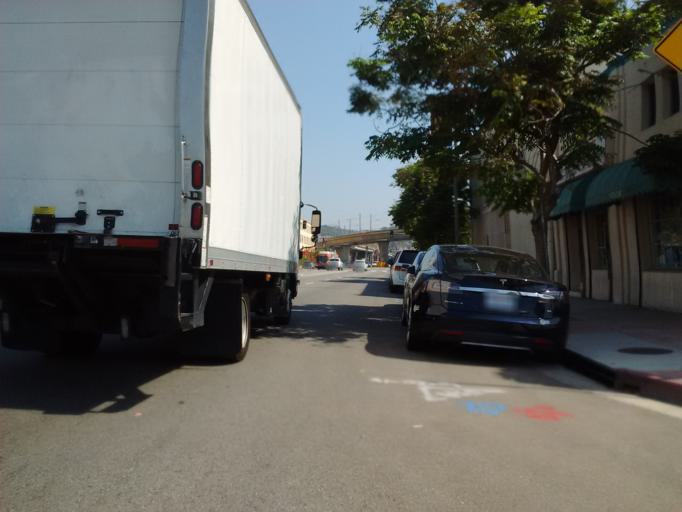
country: US
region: California
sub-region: Los Angeles County
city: Los Angeles
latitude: 34.0607
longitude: -118.2364
